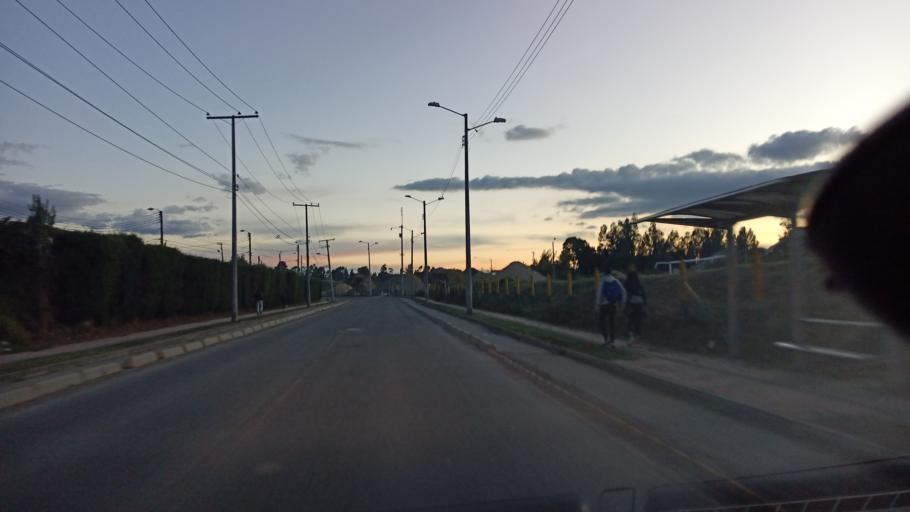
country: CO
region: Cundinamarca
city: Chia
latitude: 4.8607
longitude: -74.0665
